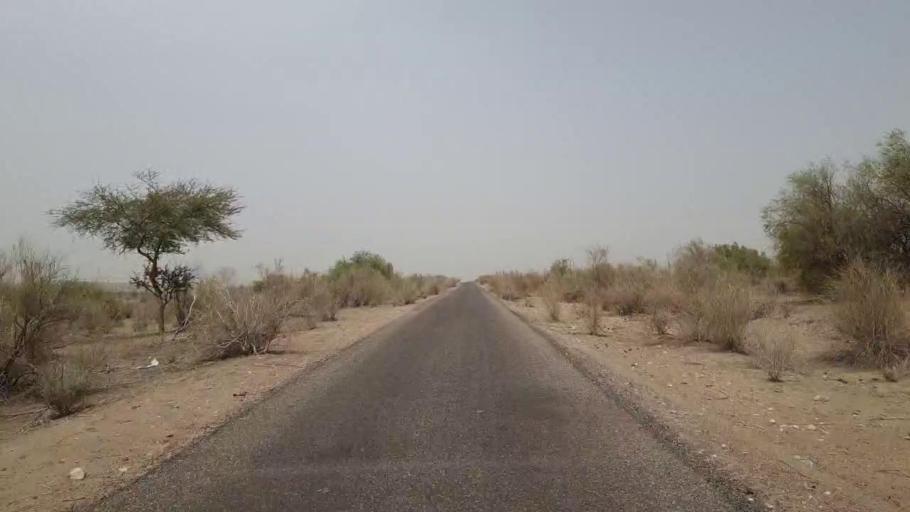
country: PK
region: Sindh
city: Islamkot
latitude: 24.7675
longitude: 70.4837
